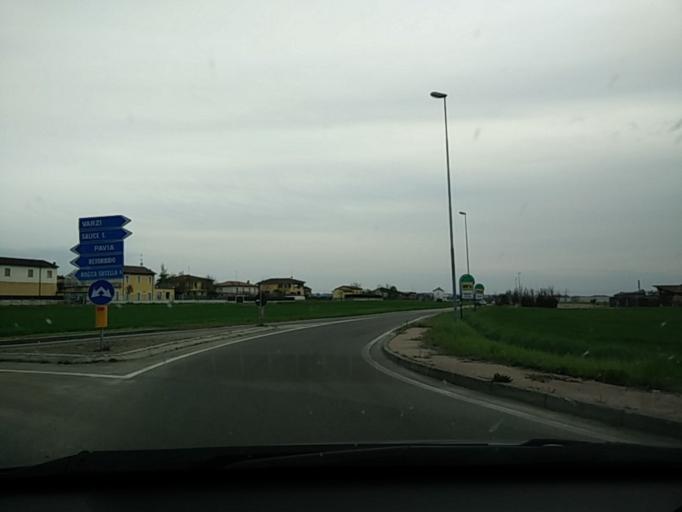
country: IT
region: Lombardy
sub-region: Provincia di Pavia
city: Retorbido
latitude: 44.9536
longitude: 9.0337
